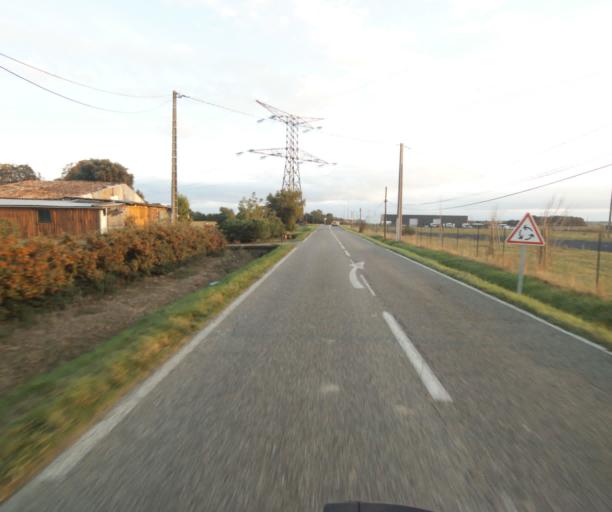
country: FR
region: Midi-Pyrenees
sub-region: Departement du Tarn-et-Garonne
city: Verdun-sur-Garonne
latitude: 43.8243
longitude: 1.2442
